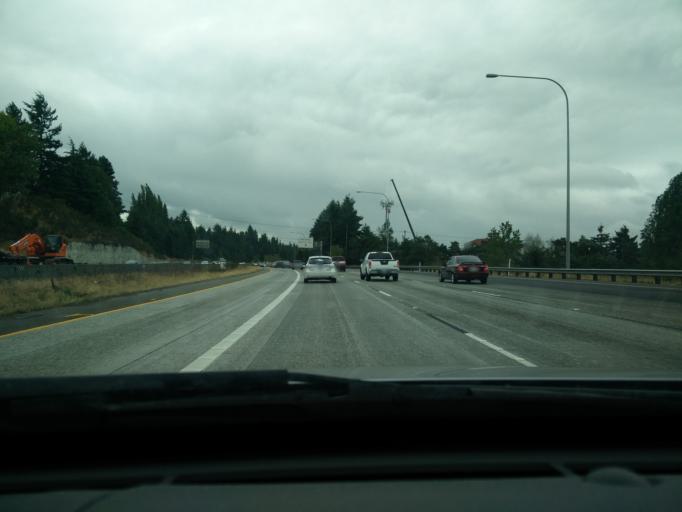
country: US
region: Washington
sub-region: King County
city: Shoreline
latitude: 47.7524
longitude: -122.3303
